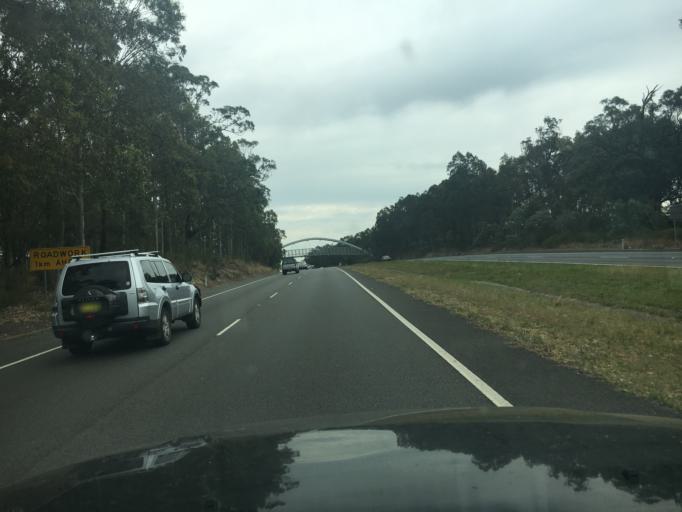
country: AU
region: New South Wales
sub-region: Maitland Municipality
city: East Maitland
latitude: -32.7699
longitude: 151.6039
